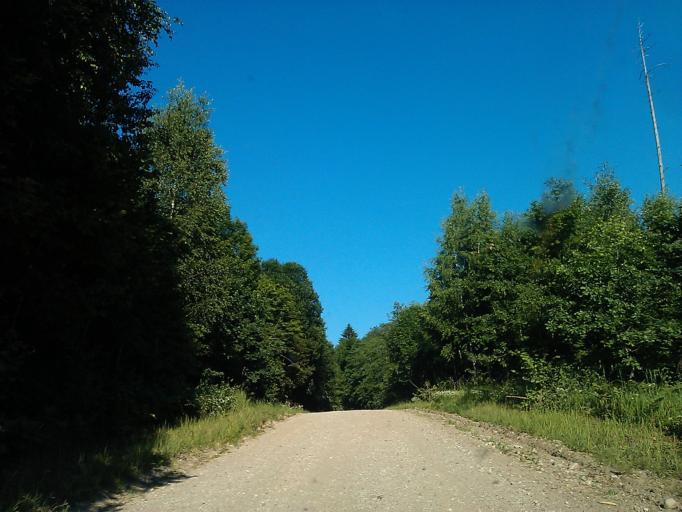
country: LV
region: Raunas
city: Rauna
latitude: 57.2577
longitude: 25.5534
